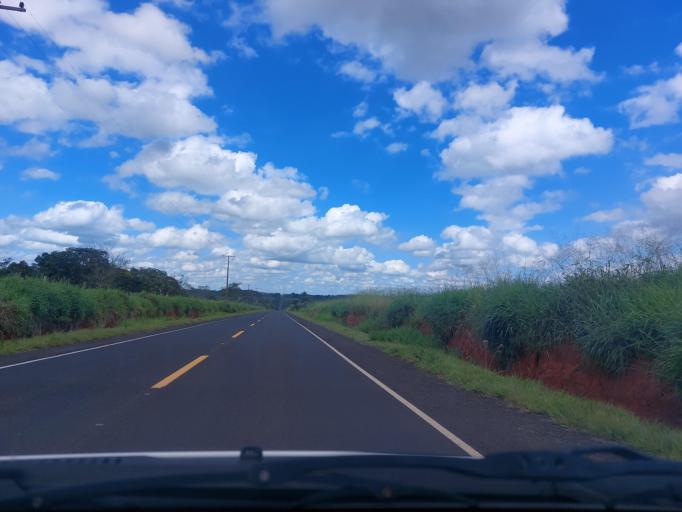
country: PY
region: San Pedro
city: Guayaybi
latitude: -24.5375
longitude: -56.5197
